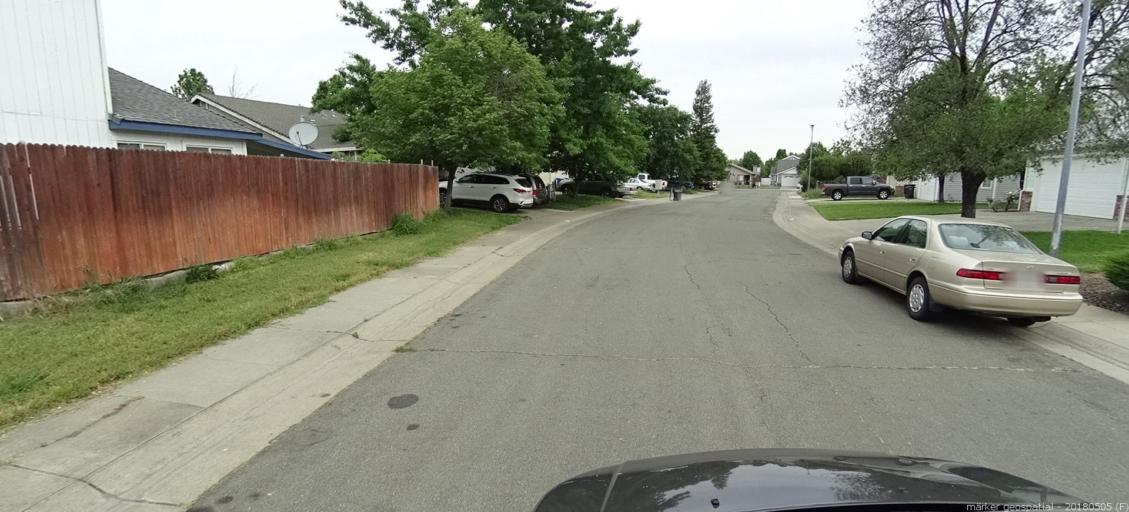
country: US
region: California
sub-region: Sacramento County
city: Rio Linda
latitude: 38.6561
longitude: -121.4460
